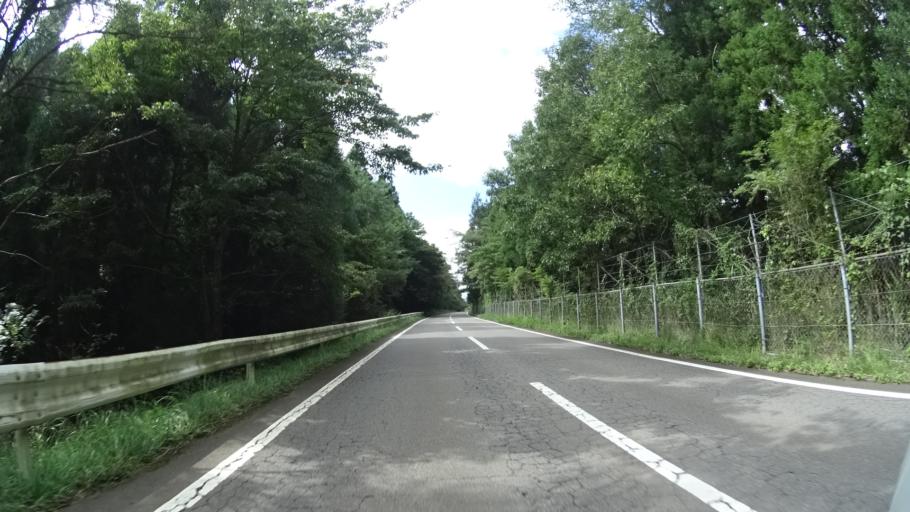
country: JP
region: Oita
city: Beppu
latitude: 33.3341
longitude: 131.4246
